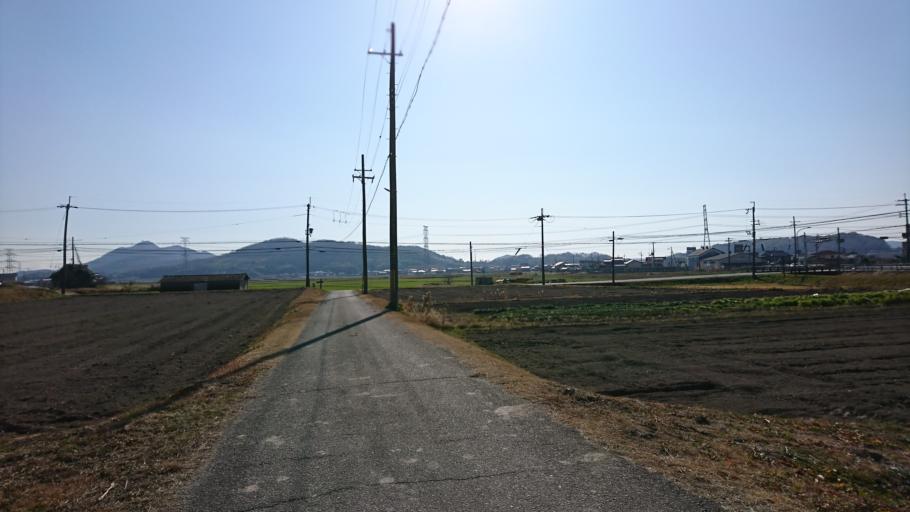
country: JP
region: Hyogo
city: Kakogawacho-honmachi
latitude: 34.8336
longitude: 134.8406
